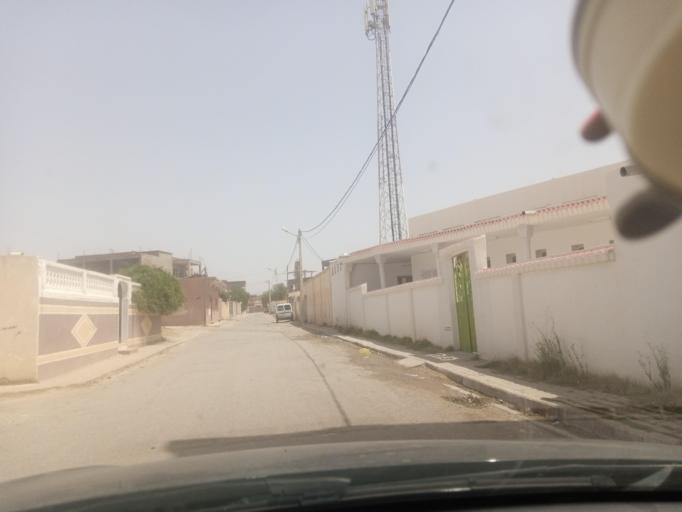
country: TN
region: Al Qasrayn
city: Kasserine
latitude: 35.2107
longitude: 8.8974
